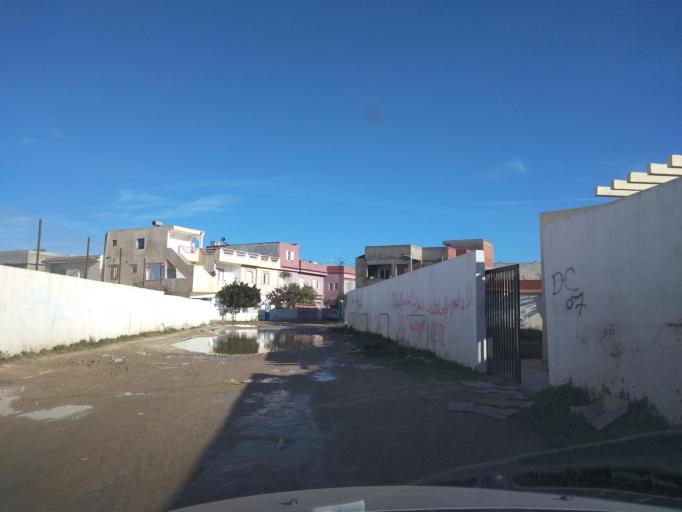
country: TN
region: Ariana
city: Qal'at al Andalus
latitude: 37.0614
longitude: 10.1209
